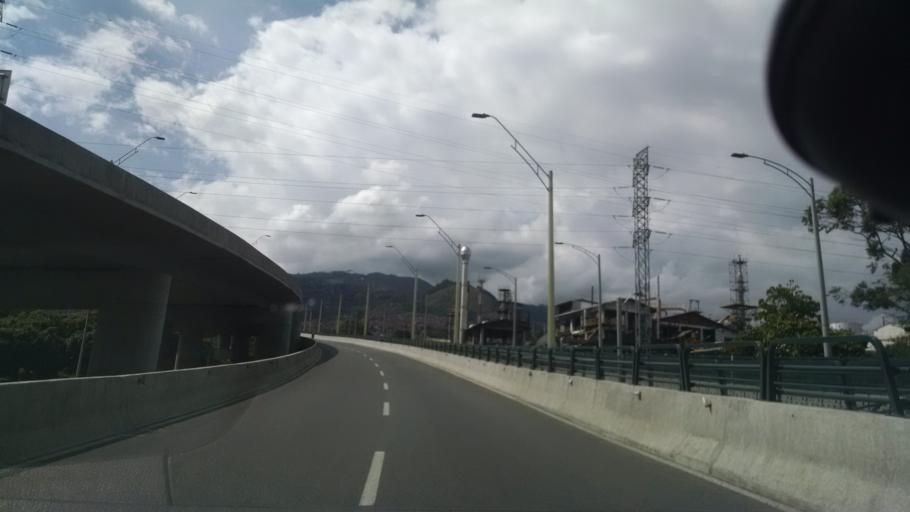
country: CO
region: Antioquia
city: Medellin
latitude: 6.2875
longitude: -75.5678
